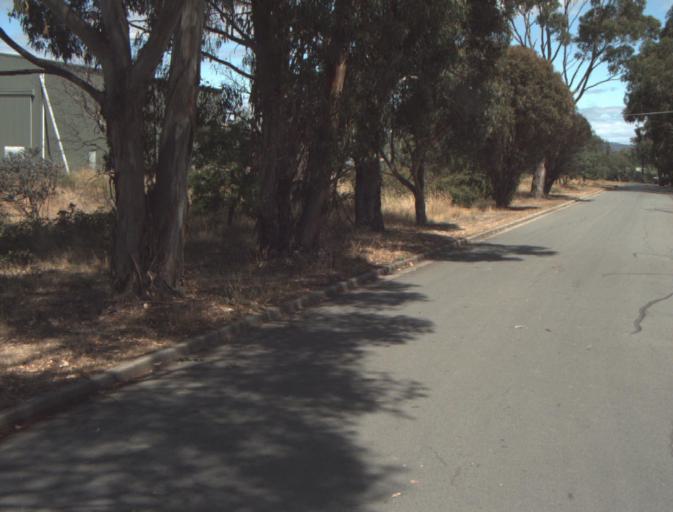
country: AU
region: Tasmania
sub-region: Launceston
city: Mayfield
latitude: -41.3736
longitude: 147.1326
